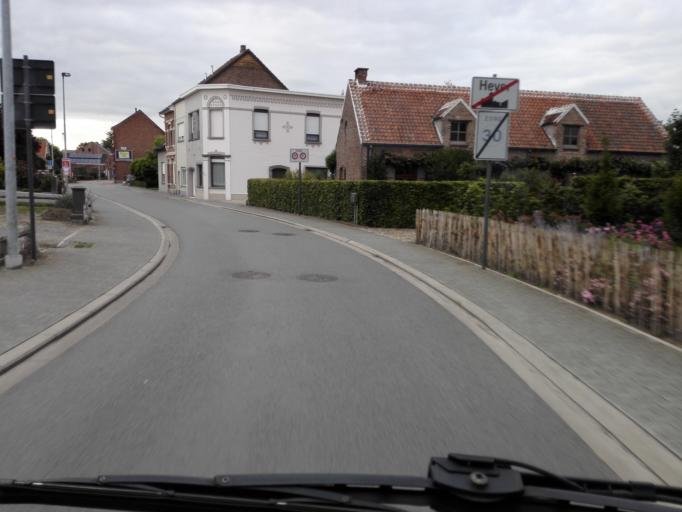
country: BE
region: Flanders
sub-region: Provincie Vlaams-Brabant
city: Boortmeerbeek
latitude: 50.9931
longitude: 4.5543
